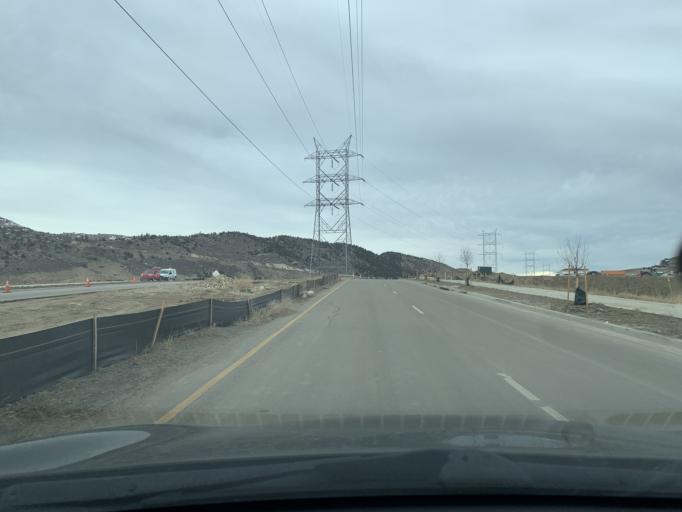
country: US
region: Colorado
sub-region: Jefferson County
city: West Pleasant View
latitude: 39.6719
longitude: -105.1812
